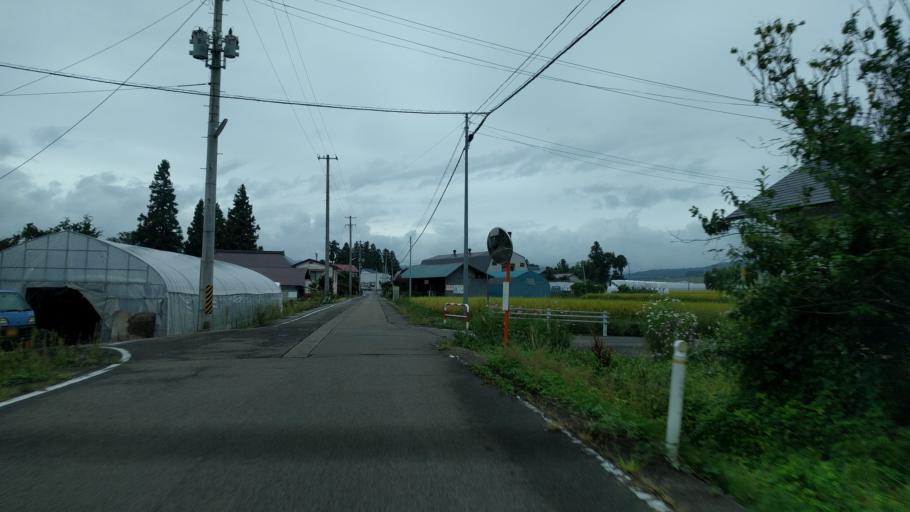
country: JP
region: Fukushima
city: Kitakata
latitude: 37.6110
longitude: 139.9146
